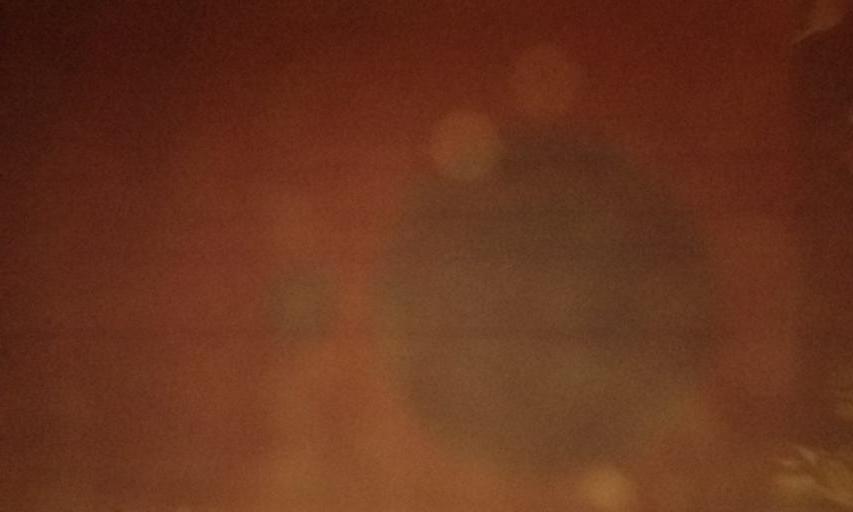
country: JP
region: Hyogo
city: Aioi
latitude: 34.8194
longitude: 134.5155
